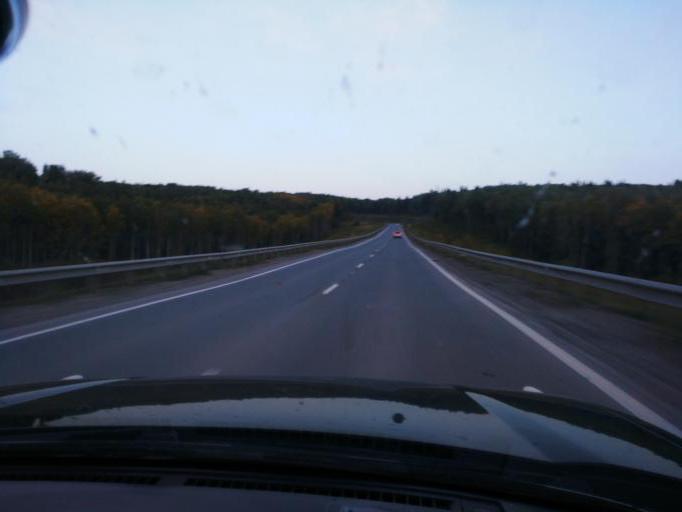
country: RU
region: Perm
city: Sylva
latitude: 58.2992
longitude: 56.7956
